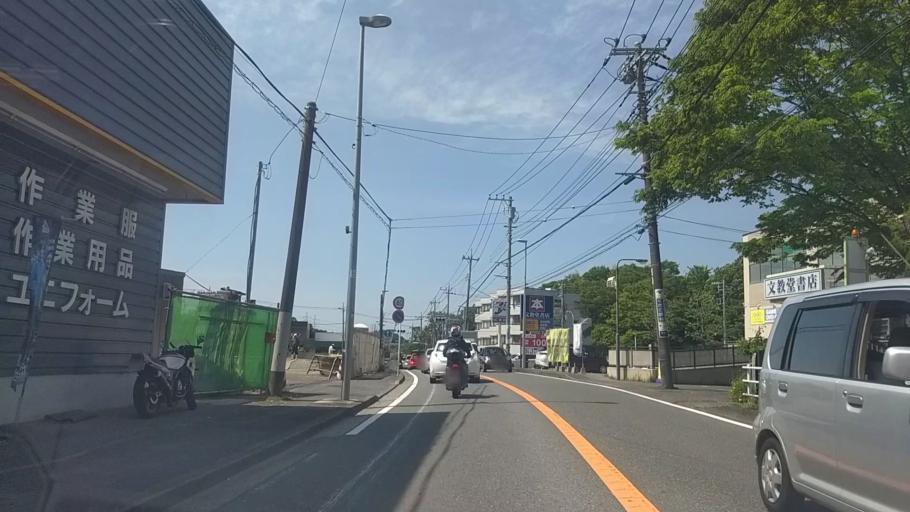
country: JP
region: Kanagawa
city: Kamakura
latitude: 35.3482
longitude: 139.5818
